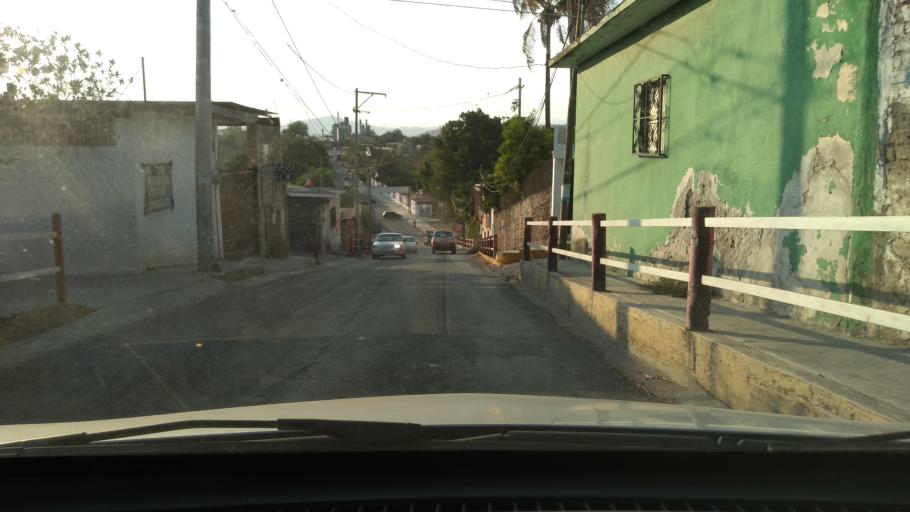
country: MX
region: Morelos
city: Puente de Ixtla
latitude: 18.6207
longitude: -99.3173
